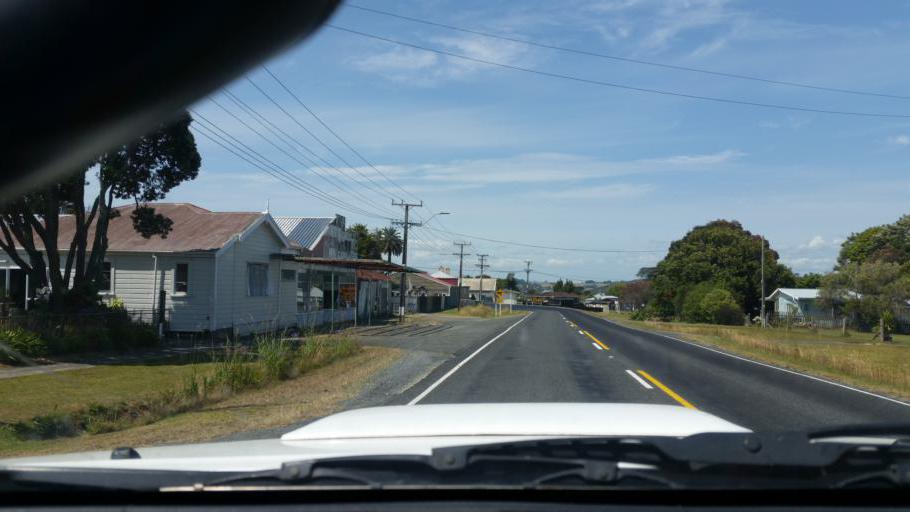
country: NZ
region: Northland
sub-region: Kaipara District
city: Dargaville
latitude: -36.0317
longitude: 173.9221
